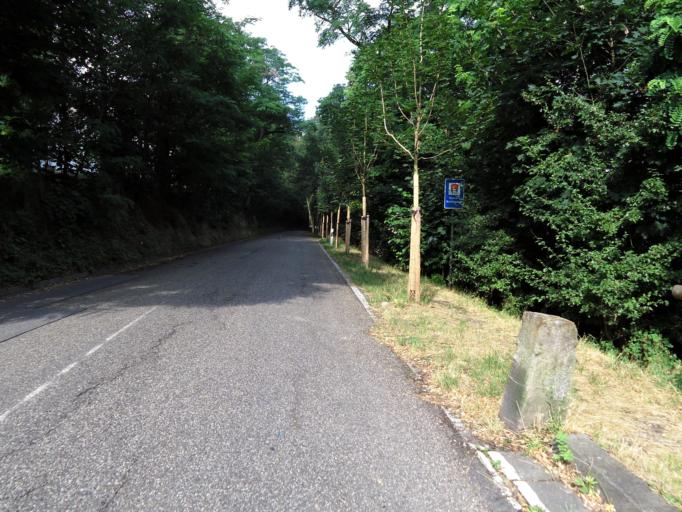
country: DE
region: Rheinland-Pfalz
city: Bad Duerkheim
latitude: 49.4551
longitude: 8.1570
